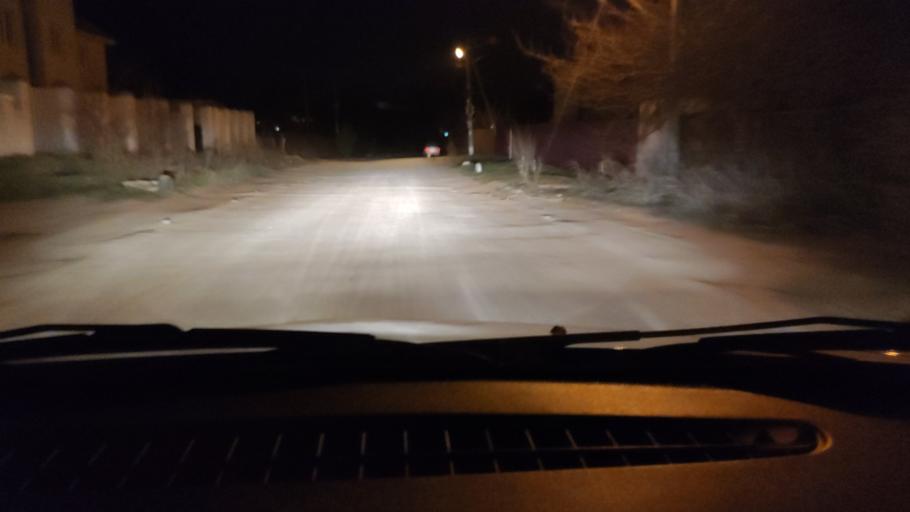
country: RU
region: Voronezj
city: Pridonskoy
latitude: 51.6365
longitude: 39.0909
